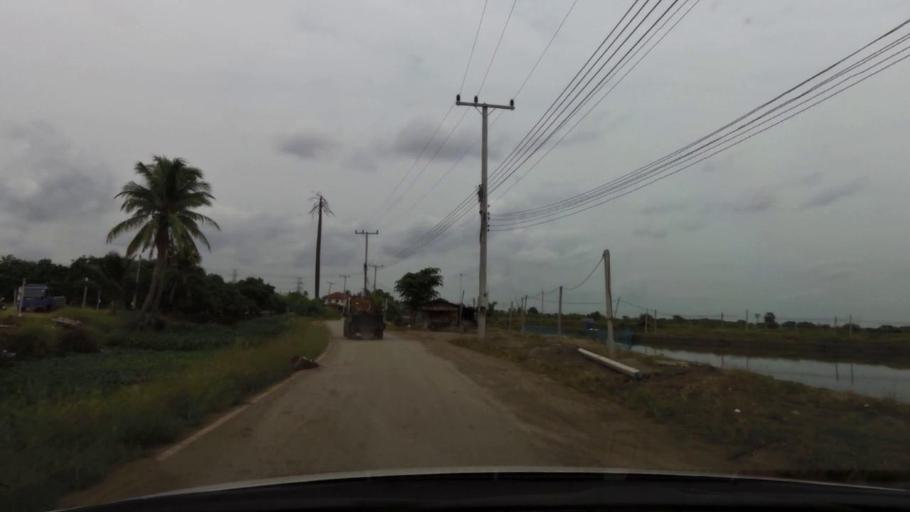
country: TH
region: Samut Sakhon
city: Ban Phaeo
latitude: 13.6208
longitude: 100.0290
